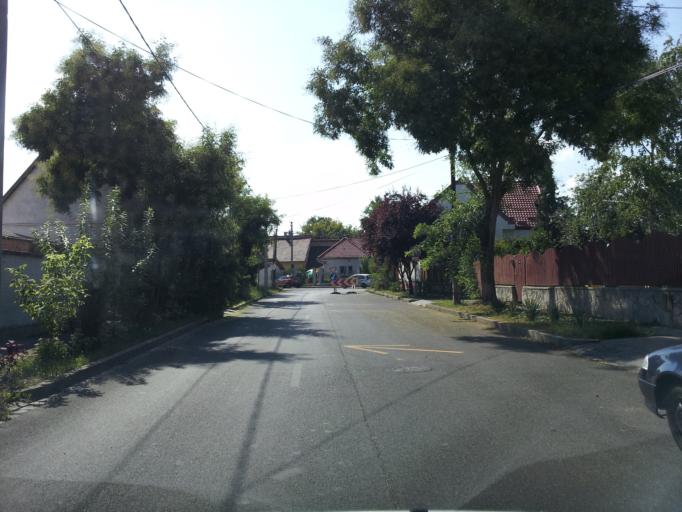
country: HU
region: Budapest
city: Budapest XXII. keruelet
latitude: 47.4205
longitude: 19.0325
